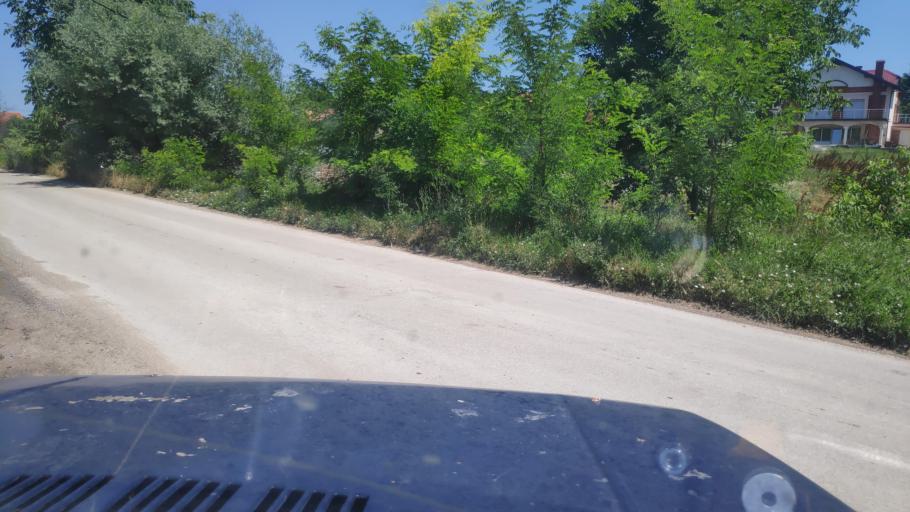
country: MK
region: Kumanovo
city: Bedinje
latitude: 42.1743
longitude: 21.6943
